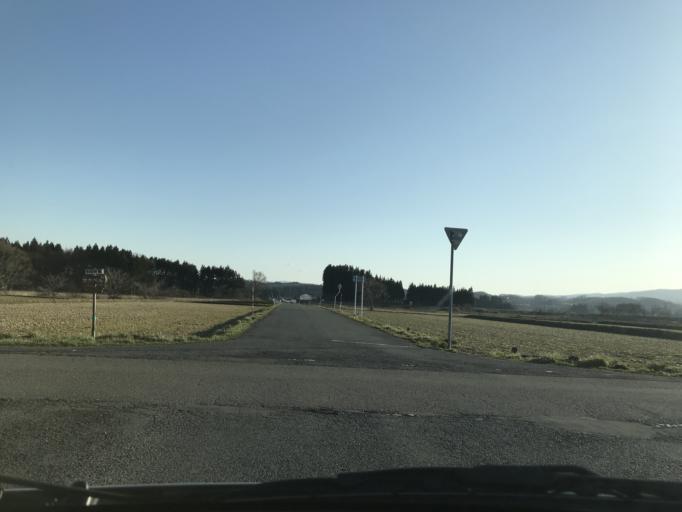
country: JP
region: Iwate
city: Kitakami
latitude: 39.2169
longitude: 141.0393
